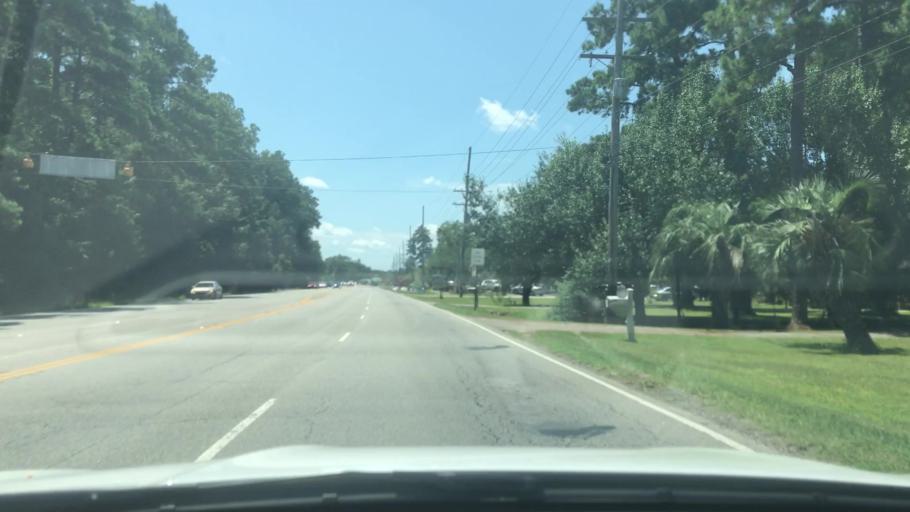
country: US
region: South Carolina
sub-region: Horry County
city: Conway
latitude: 33.8716
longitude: -79.0518
